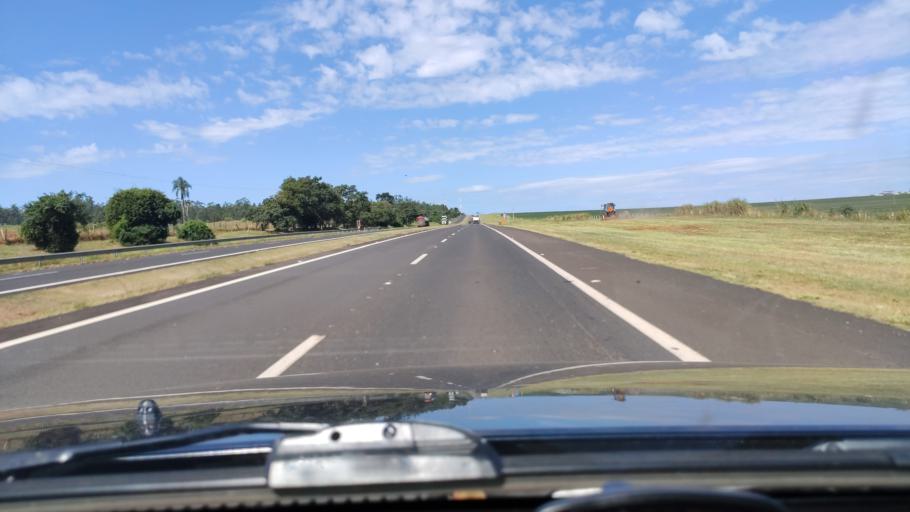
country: BR
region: Sao Paulo
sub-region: Rancharia
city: Rancharia
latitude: -22.4212
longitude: -51.0329
